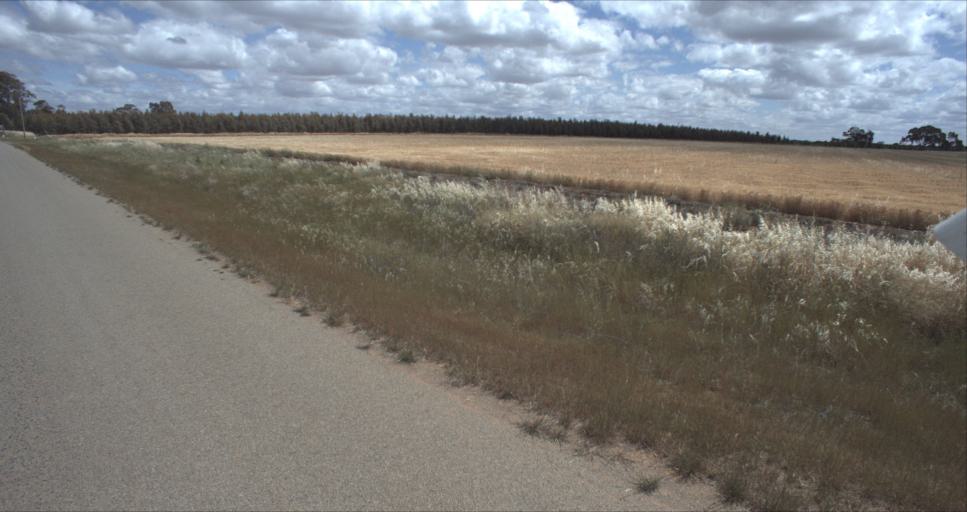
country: AU
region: New South Wales
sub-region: Leeton
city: Leeton
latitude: -34.5726
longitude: 146.3988
